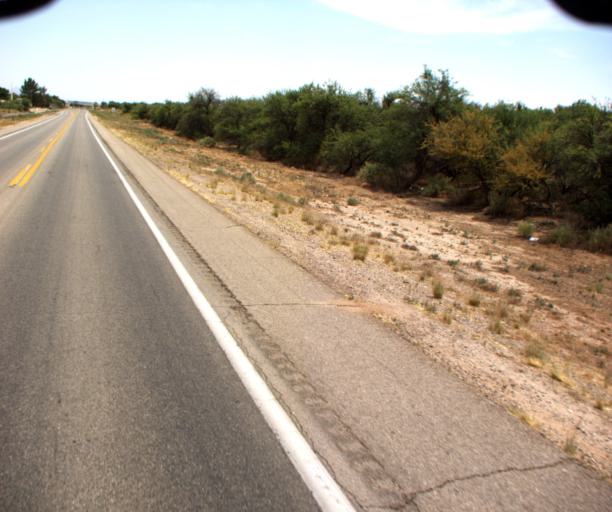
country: US
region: Arizona
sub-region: Graham County
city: Bylas
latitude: 33.0390
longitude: -109.9707
